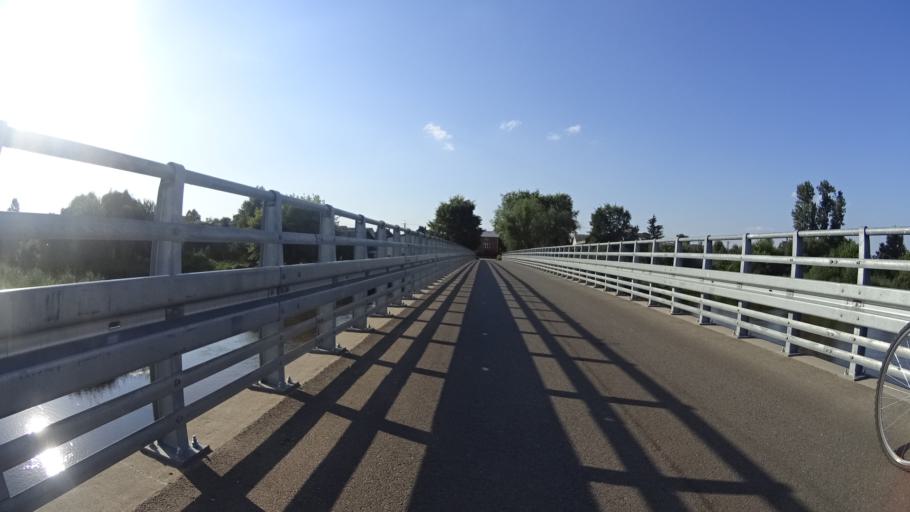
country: PL
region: Masovian Voivodeship
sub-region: Powiat bialobrzeski
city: Wysmierzyce
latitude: 51.6550
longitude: 20.8276
